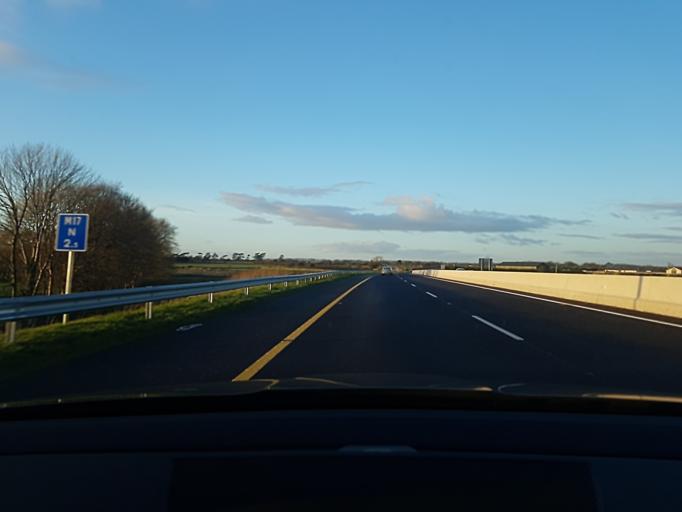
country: IE
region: Connaught
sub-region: County Galway
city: Athenry
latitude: 53.3188
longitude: -8.8016
